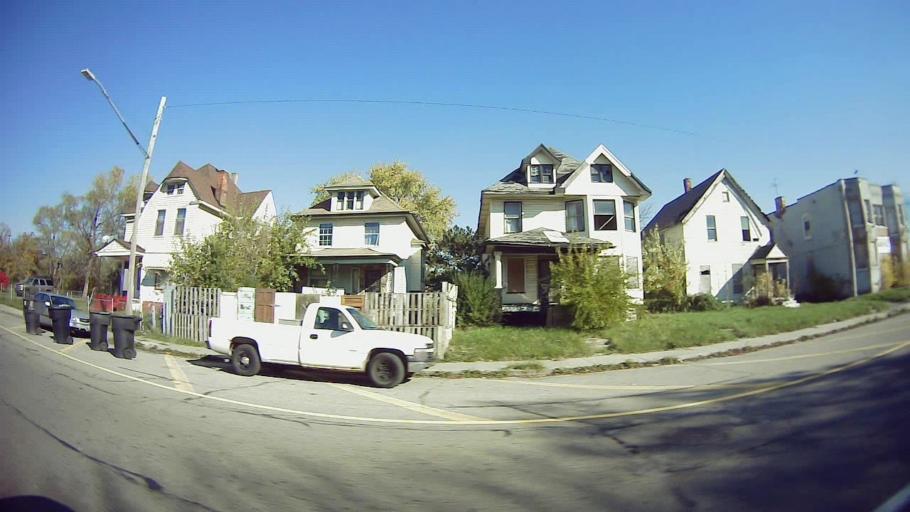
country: US
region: Michigan
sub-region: Wayne County
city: Detroit
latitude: 42.3548
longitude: -83.0898
